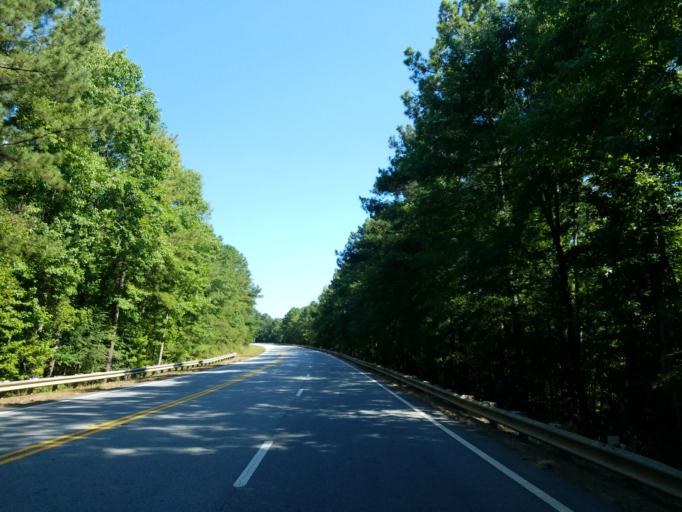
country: US
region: Georgia
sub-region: Crawford County
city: Roberta
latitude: 32.8266
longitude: -84.0603
